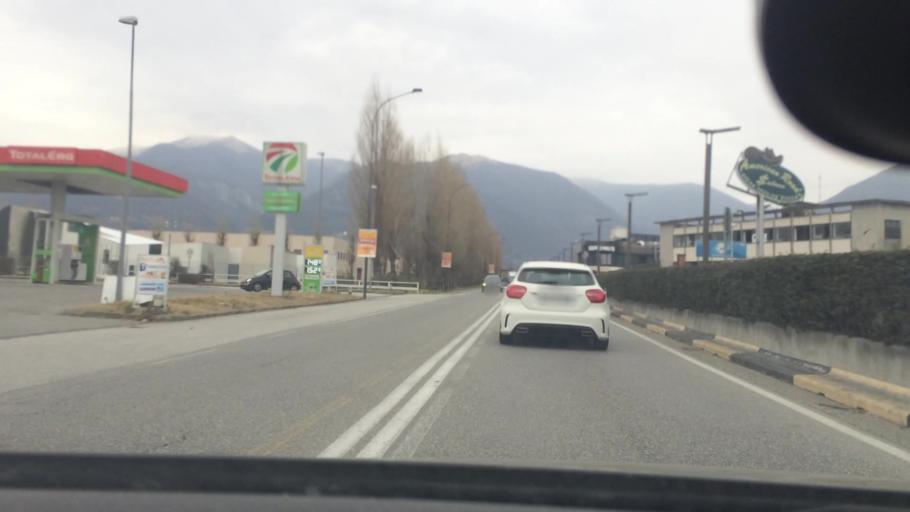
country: IT
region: Lombardy
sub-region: Provincia di Como
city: Merone
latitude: 45.7989
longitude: 9.2391
